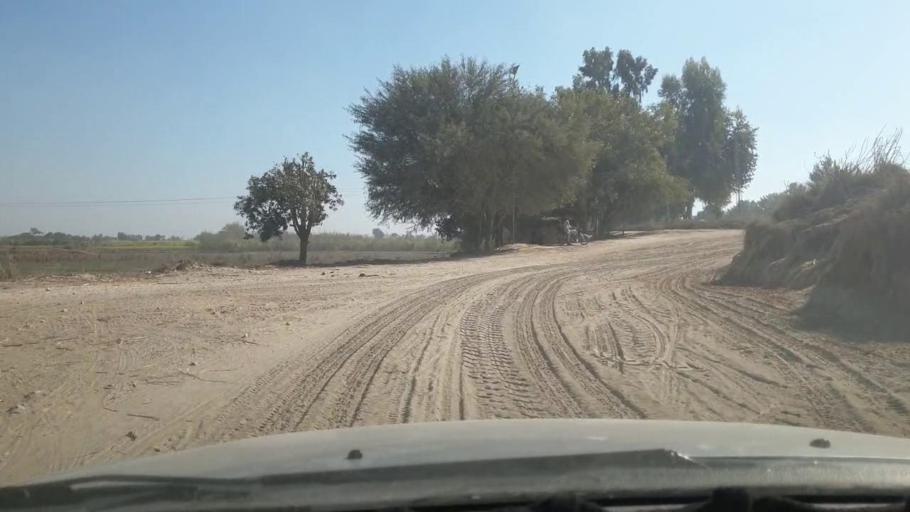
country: PK
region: Sindh
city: Ghotki
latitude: 28.0129
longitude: 69.2321
